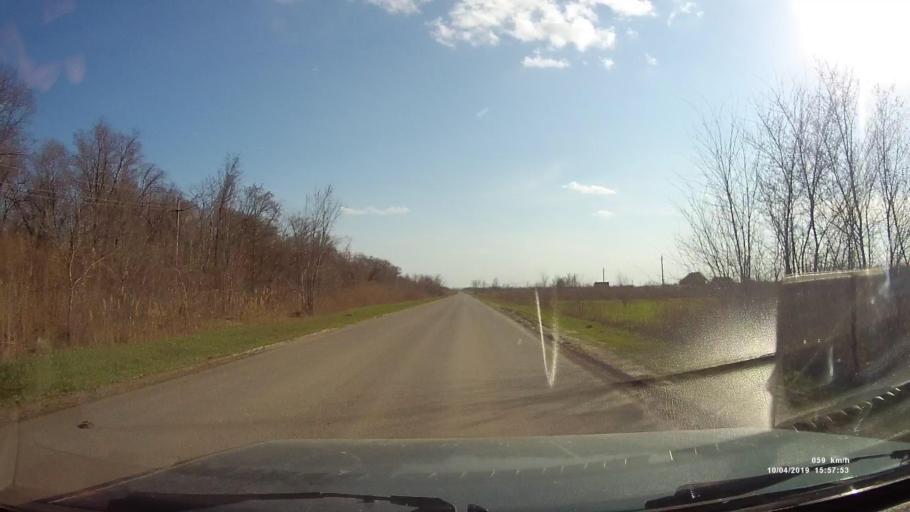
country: RU
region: Rostov
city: Masalovka
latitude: 48.4076
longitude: 40.2744
